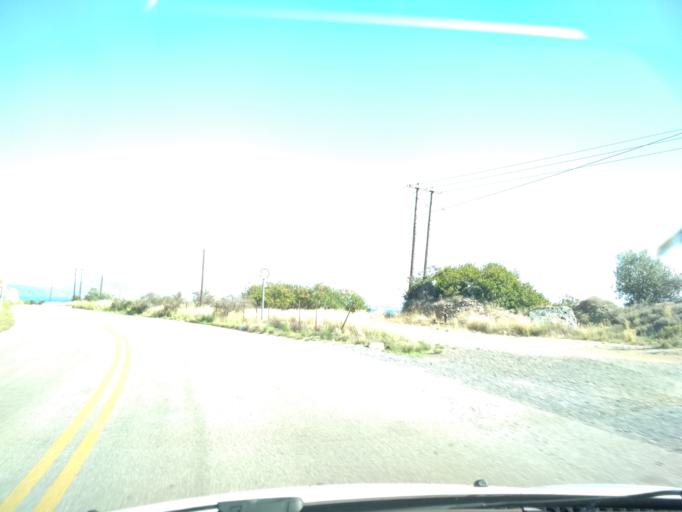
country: GR
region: Central Greece
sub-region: Nomos Evvoias
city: Oreoi
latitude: 38.8424
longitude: 23.0961
